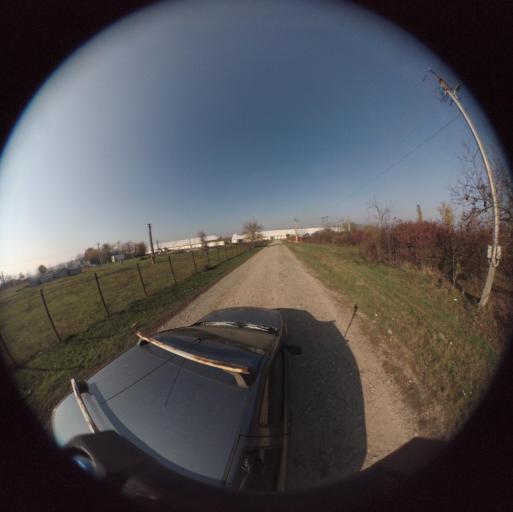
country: RO
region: Vaslui
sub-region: Comuna Dumesti
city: Dumesti
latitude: 46.8293
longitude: 27.2643
